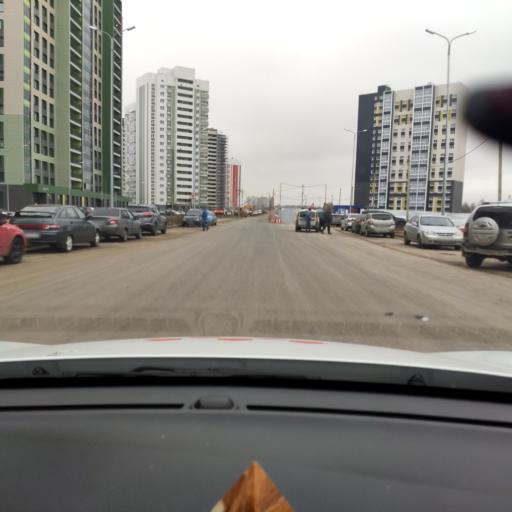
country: RU
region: Tatarstan
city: Osinovo
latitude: 55.8575
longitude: 48.9061
